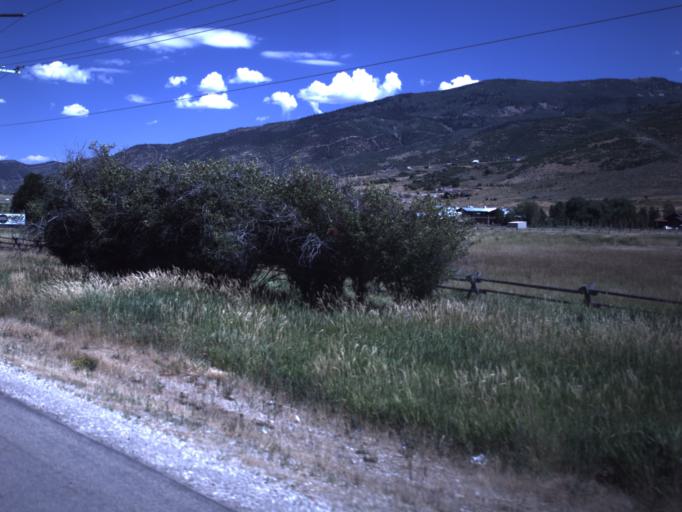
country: US
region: Utah
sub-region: Summit County
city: Kamas
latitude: 40.6556
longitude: -111.2808
